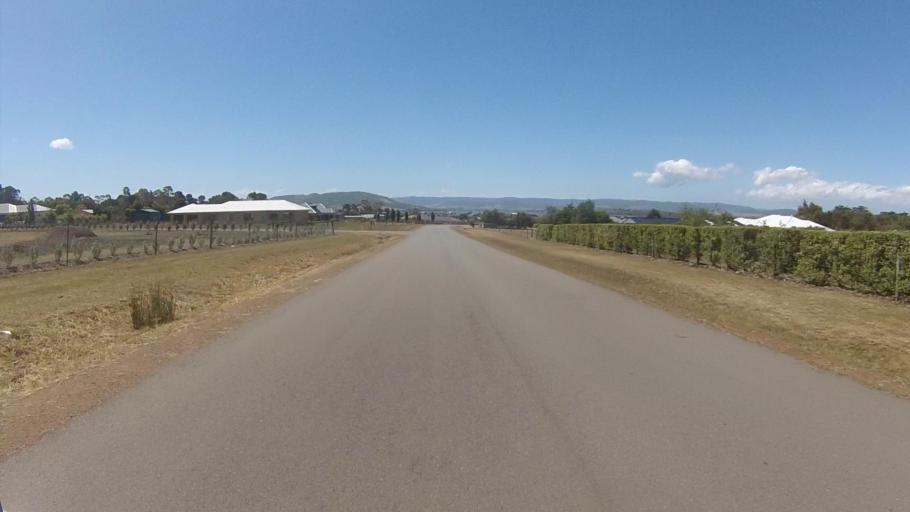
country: AU
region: Tasmania
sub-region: Clarence
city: Cambridge
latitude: -42.8446
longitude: 147.4663
